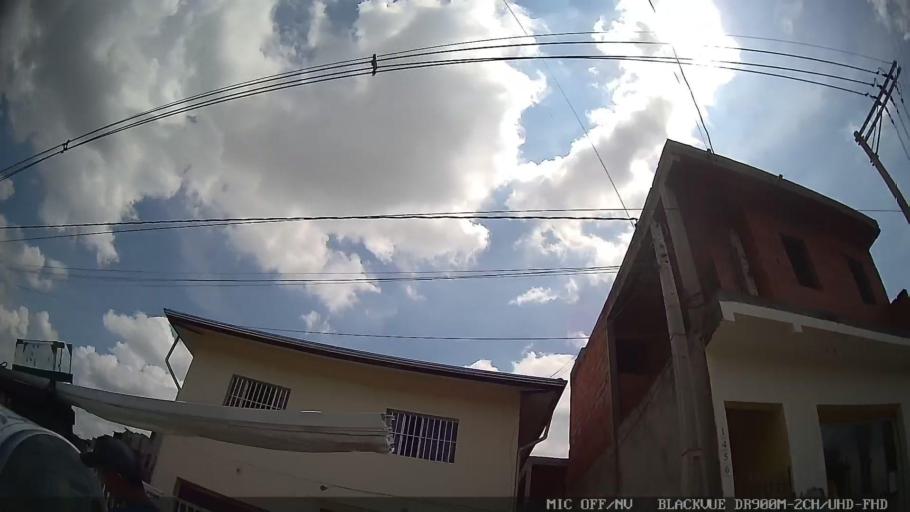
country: BR
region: Sao Paulo
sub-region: Itatiba
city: Itatiba
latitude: -23.0131
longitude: -46.8090
